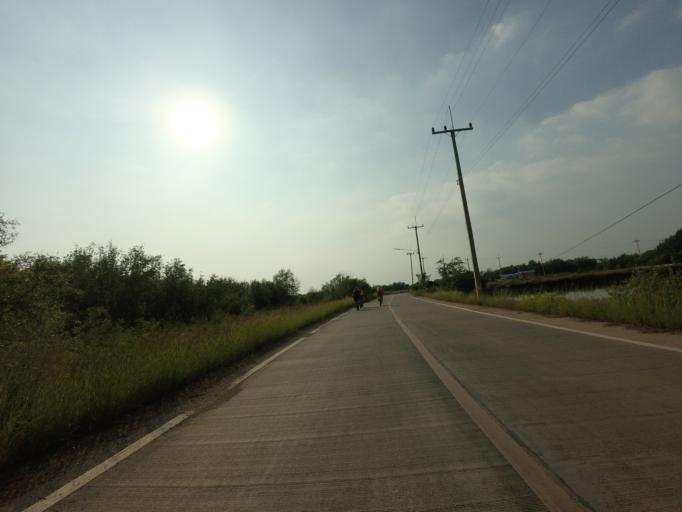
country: TH
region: Samut Sakhon
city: Samut Sakhon
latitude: 13.4976
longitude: 100.3320
